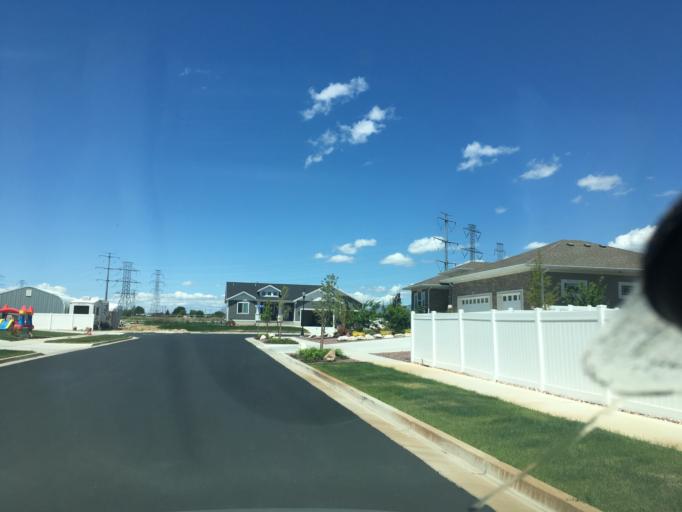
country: US
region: Utah
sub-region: Davis County
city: Layton
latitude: 41.0519
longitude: -112.0061
